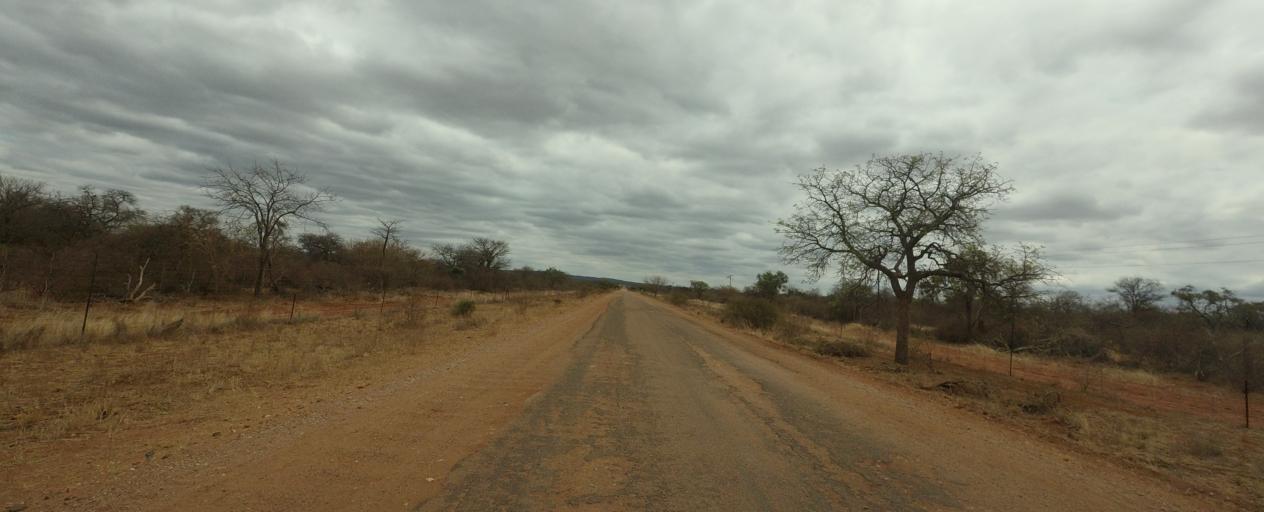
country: BW
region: Central
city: Mathathane
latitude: -22.7400
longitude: 28.4855
